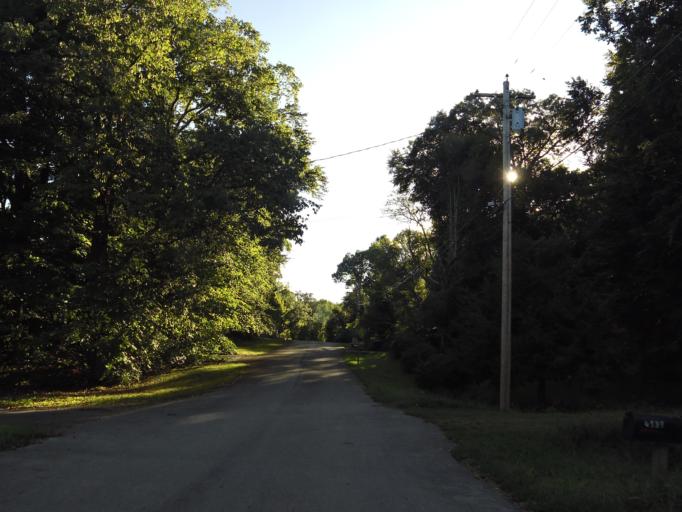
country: US
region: Tennessee
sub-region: Blount County
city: Eagleton Village
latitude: 35.8627
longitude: -83.9570
